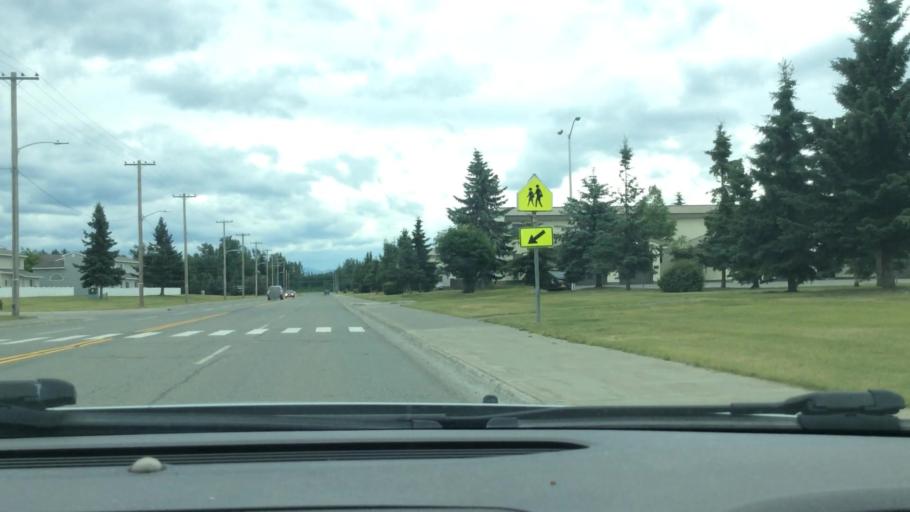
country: US
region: Alaska
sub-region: Anchorage Municipality
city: Anchorage
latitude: 61.2334
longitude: -149.8493
